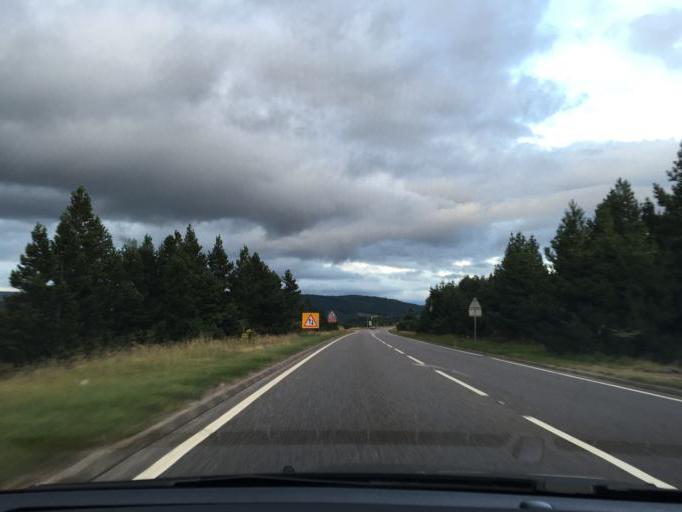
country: GB
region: Scotland
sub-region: Highland
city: Inverness
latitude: 57.3860
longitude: -4.0865
